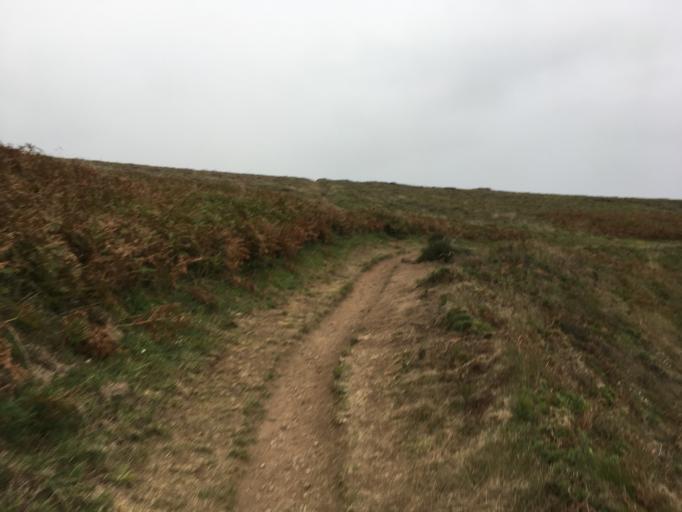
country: FR
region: Brittany
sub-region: Departement du Finistere
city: Plogoff
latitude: 48.0524
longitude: -4.7086
